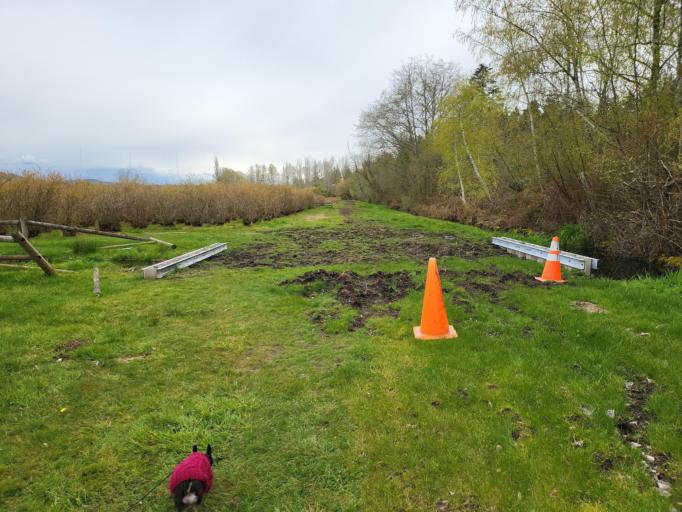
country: US
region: Washington
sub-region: King County
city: Bellevue
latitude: 47.5925
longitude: -122.1911
